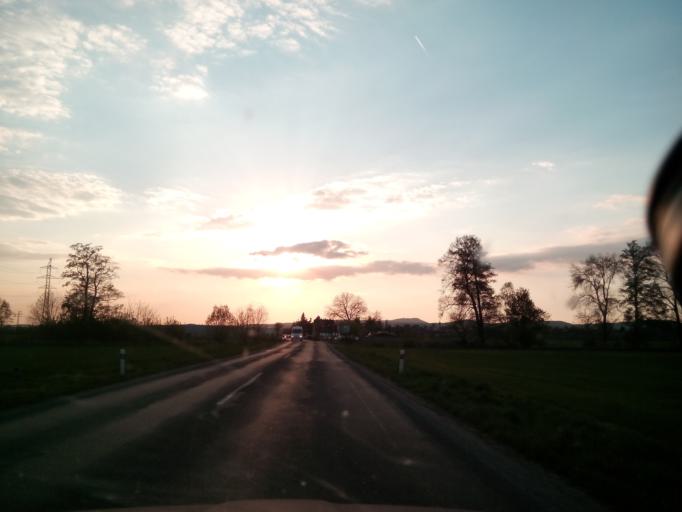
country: SK
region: Trnavsky
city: Vrbove
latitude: 48.5887
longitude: 17.7625
